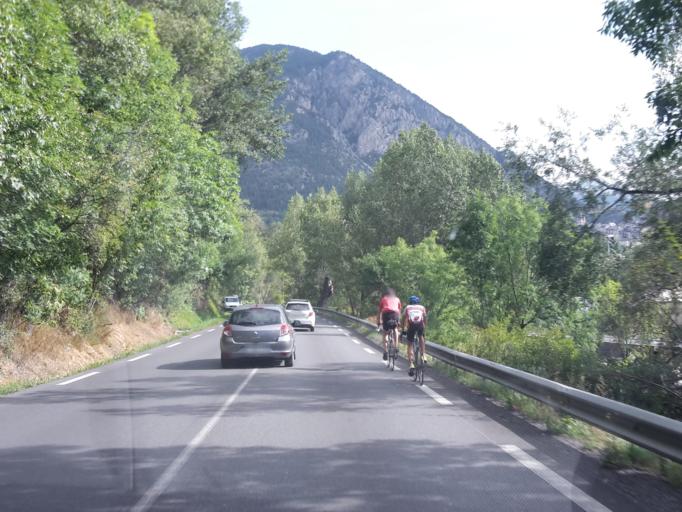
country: FR
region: Provence-Alpes-Cote d'Azur
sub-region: Departement des Hautes-Alpes
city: Briancon
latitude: 44.8913
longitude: 6.6287
